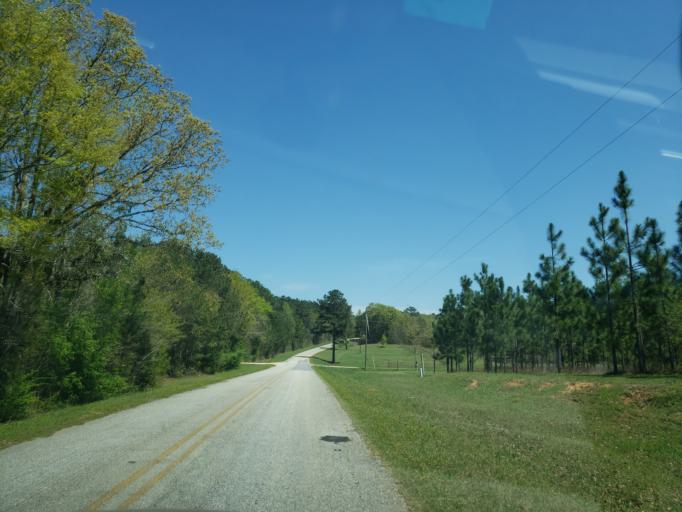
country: US
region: Alabama
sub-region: Tallapoosa County
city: Camp Hill
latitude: 32.6706
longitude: -85.7096
